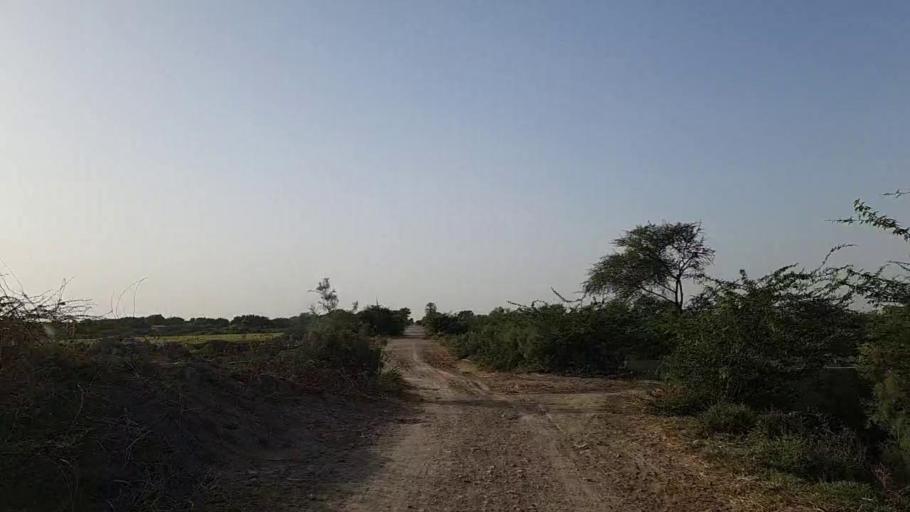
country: PK
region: Sindh
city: Jati
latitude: 24.3433
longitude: 68.1456
